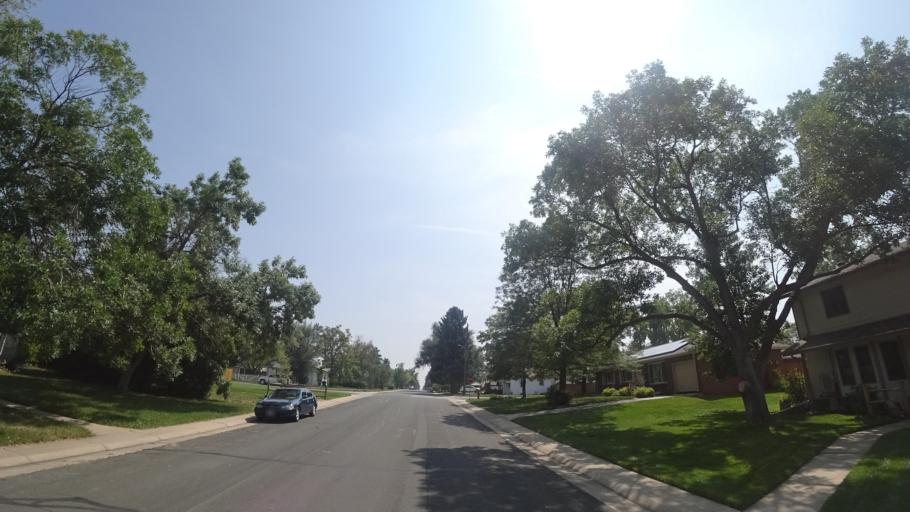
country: US
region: Colorado
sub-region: Arapahoe County
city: Englewood
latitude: 39.6318
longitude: -104.9961
